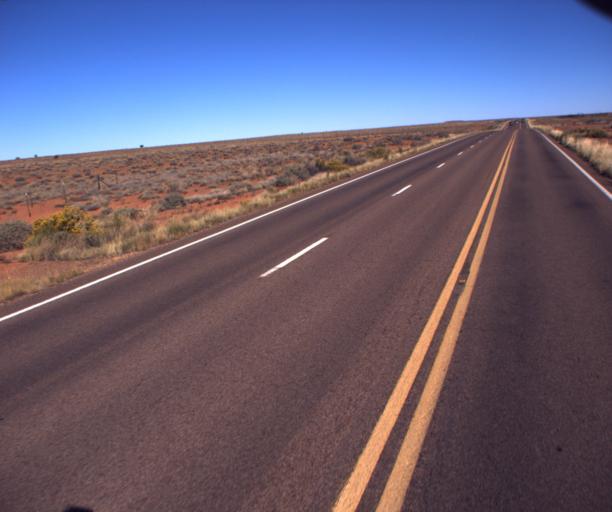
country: US
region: Arizona
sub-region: Navajo County
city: Snowflake
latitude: 34.7052
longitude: -110.1099
